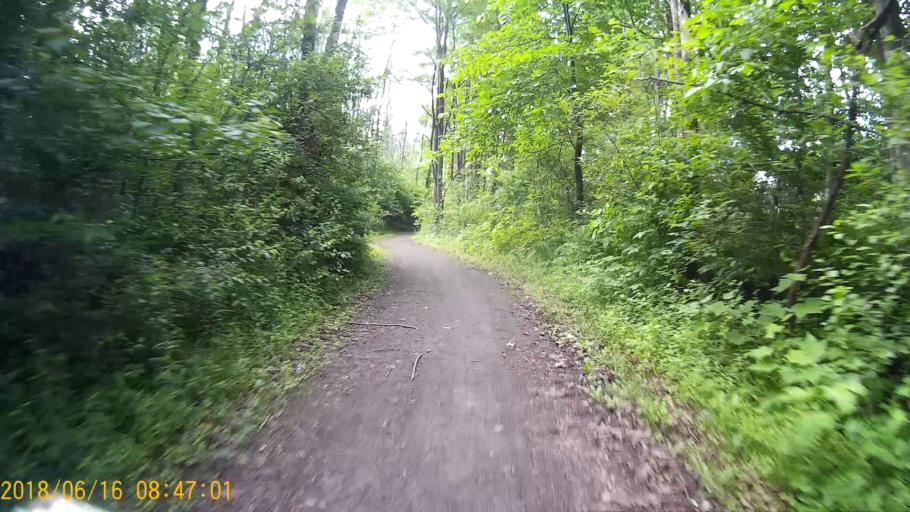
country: CA
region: Ontario
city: Bells Corners
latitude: 45.3451
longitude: -75.8923
